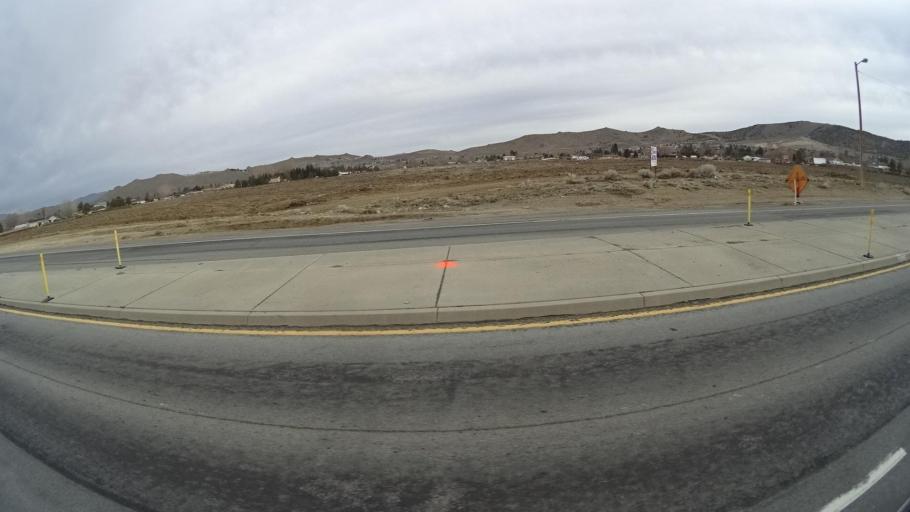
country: US
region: Nevada
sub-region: Washoe County
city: Golden Valley
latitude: 39.6075
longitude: -119.8241
